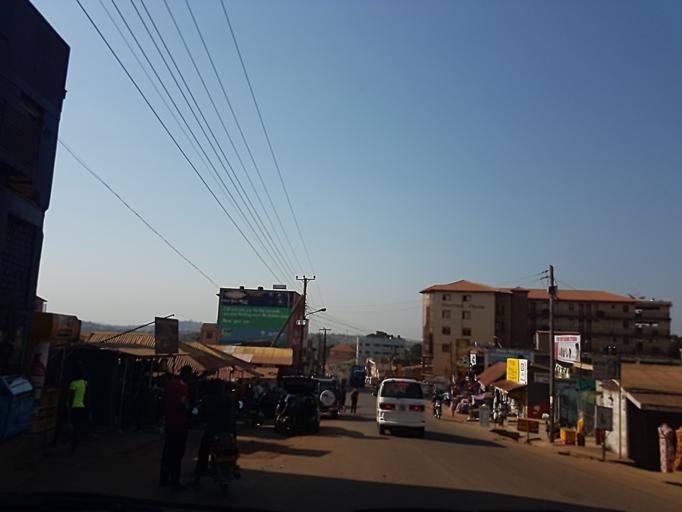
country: UG
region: Central Region
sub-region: Wakiso District
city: Kireka
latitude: 0.3554
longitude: 32.6138
